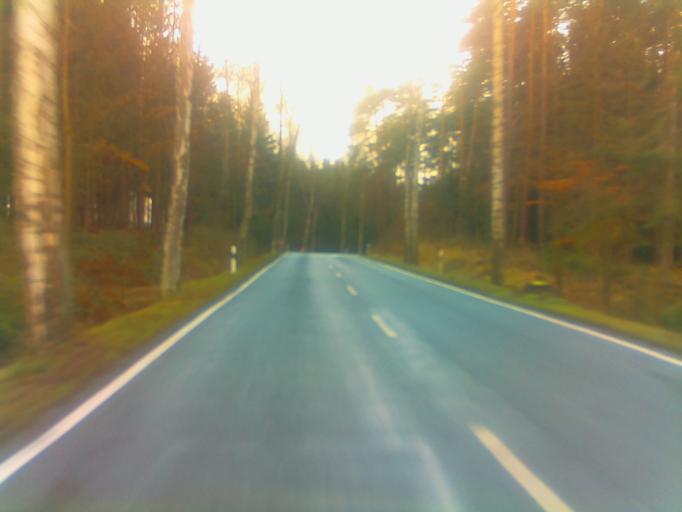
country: DE
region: Thuringia
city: Trockenborn-Wolfersdorf
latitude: 50.7535
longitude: 11.7079
